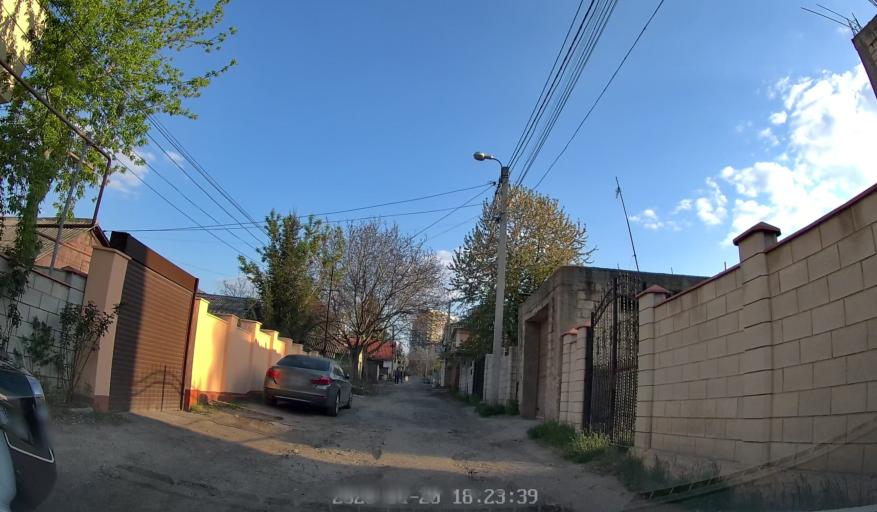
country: MD
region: Chisinau
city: Chisinau
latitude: 46.9953
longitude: 28.8377
